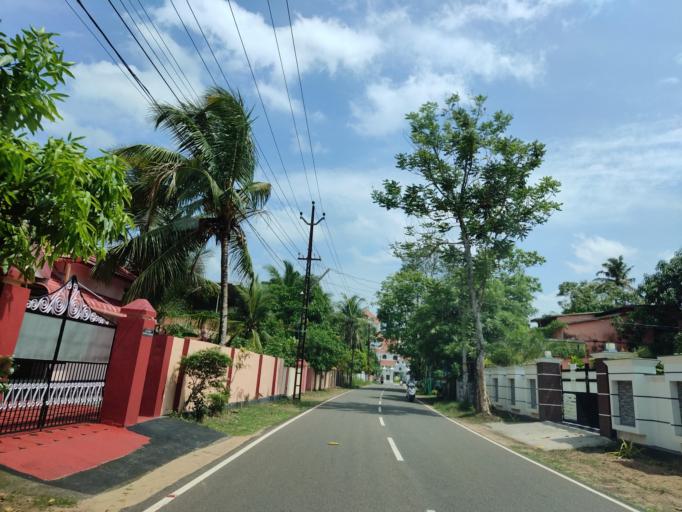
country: IN
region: Kerala
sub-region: Alappuzha
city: Mavelikara
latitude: 9.2785
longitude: 76.5679
